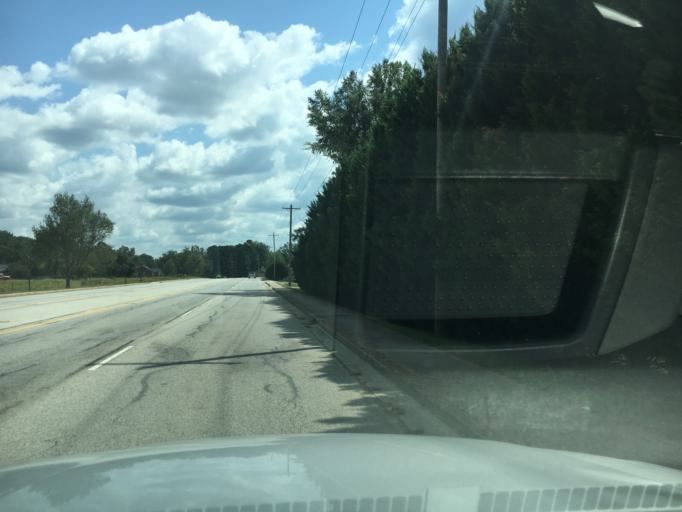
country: US
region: South Carolina
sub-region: Greenwood County
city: Greenwood
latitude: 34.1994
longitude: -82.1957
